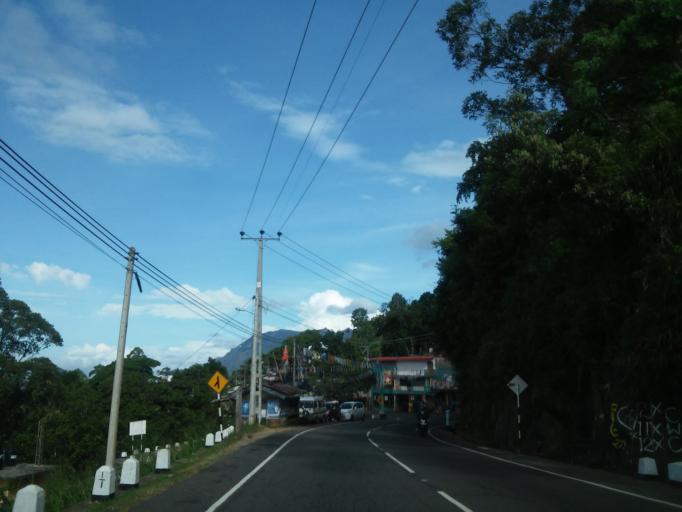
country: LK
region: Uva
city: Haputale
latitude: 6.7637
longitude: 80.9140
